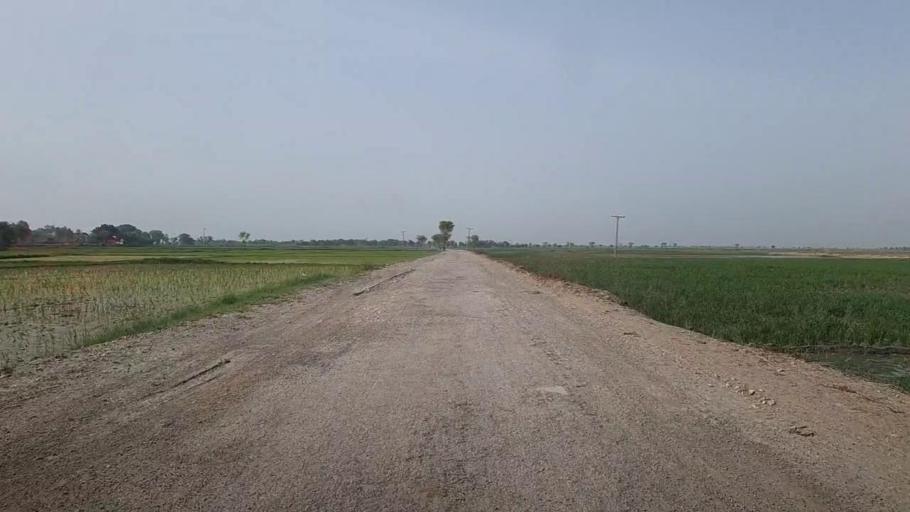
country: PK
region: Sindh
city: Mehar
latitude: 27.1126
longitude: 67.8199
